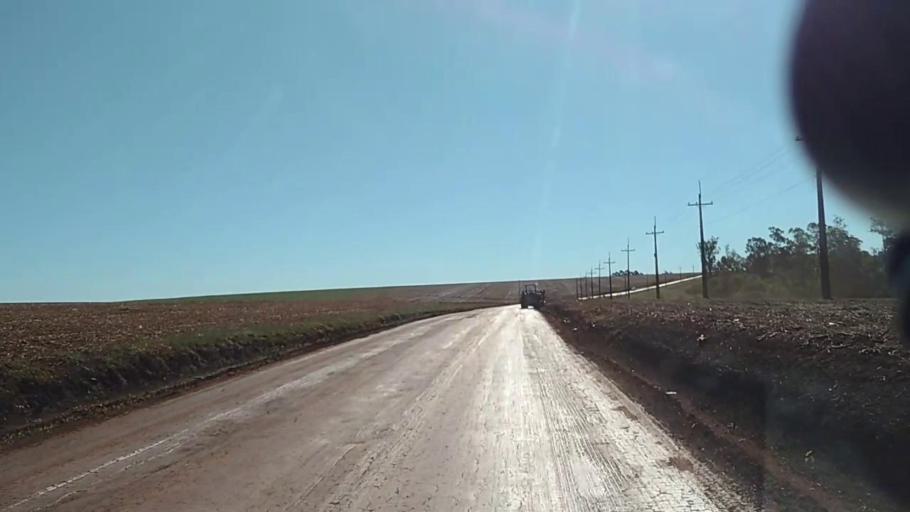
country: PY
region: Alto Parana
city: Naranjal
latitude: -25.9703
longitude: -55.2388
